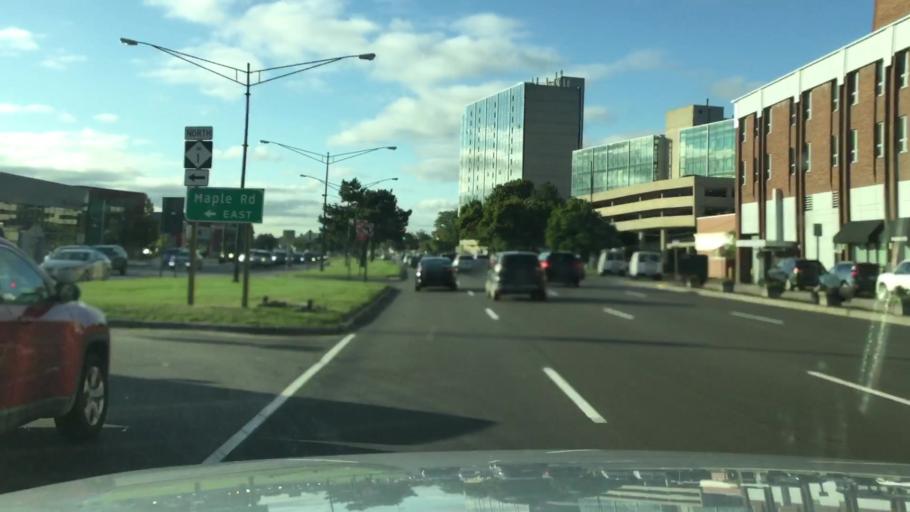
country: US
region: Michigan
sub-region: Oakland County
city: Birmingham
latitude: 42.5448
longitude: -83.2105
